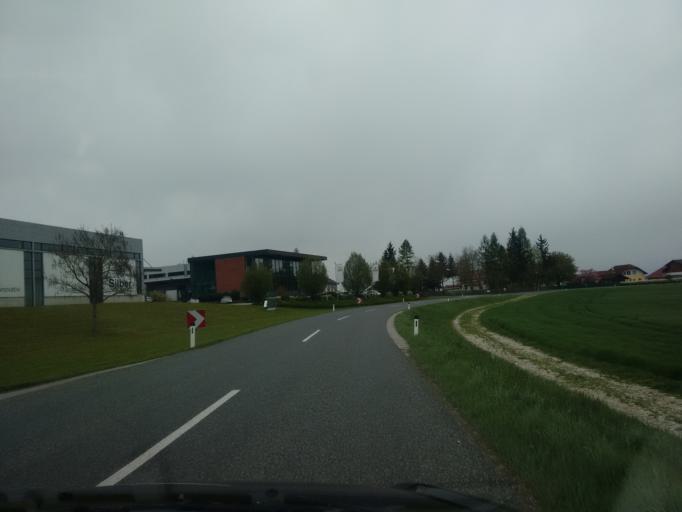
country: AT
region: Upper Austria
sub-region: Wels-Land
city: Holzhausen
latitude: 48.2385
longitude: 14.0675
